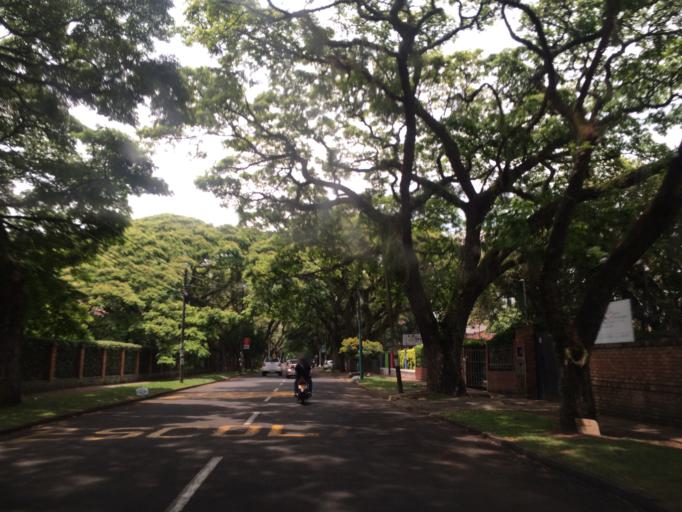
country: CO
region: Valle del Cauca
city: Cali
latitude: 3.4096
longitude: -76.5520
